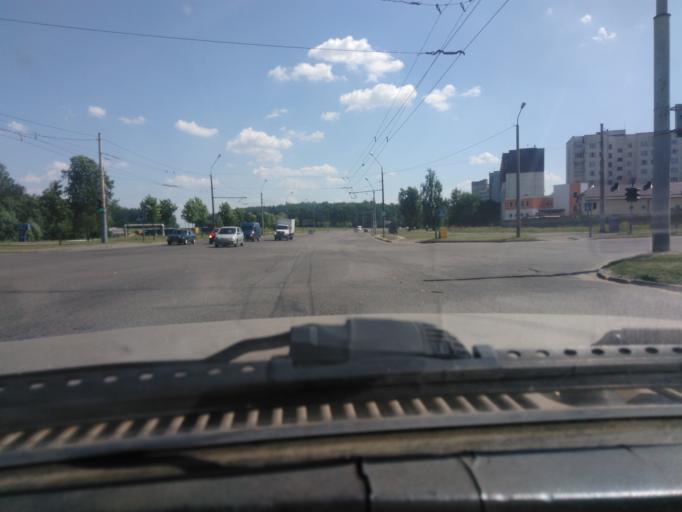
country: BY
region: Mogilev
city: Palykavichy Pyershyya
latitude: 53.9594
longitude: 30.3620
